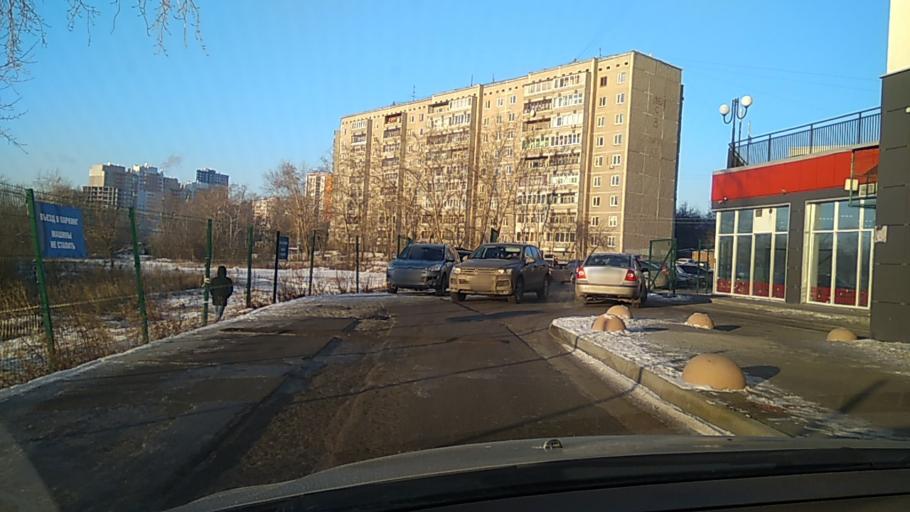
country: RU
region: Sverdlovsk
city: Yekaterinburg
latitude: 56.7825
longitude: 60.6654
